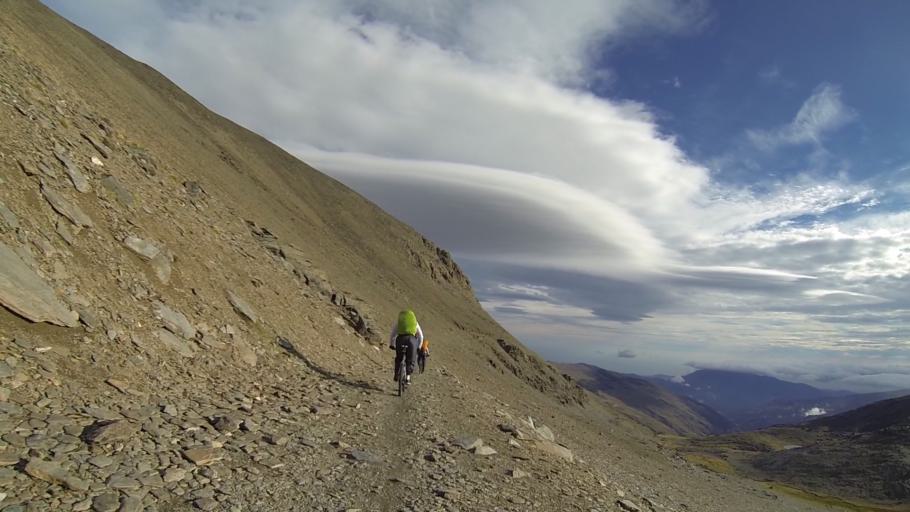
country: ES
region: Andalusia
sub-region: Provincia de Granada
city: Trevelez
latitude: 37.0518
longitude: -3.3218
